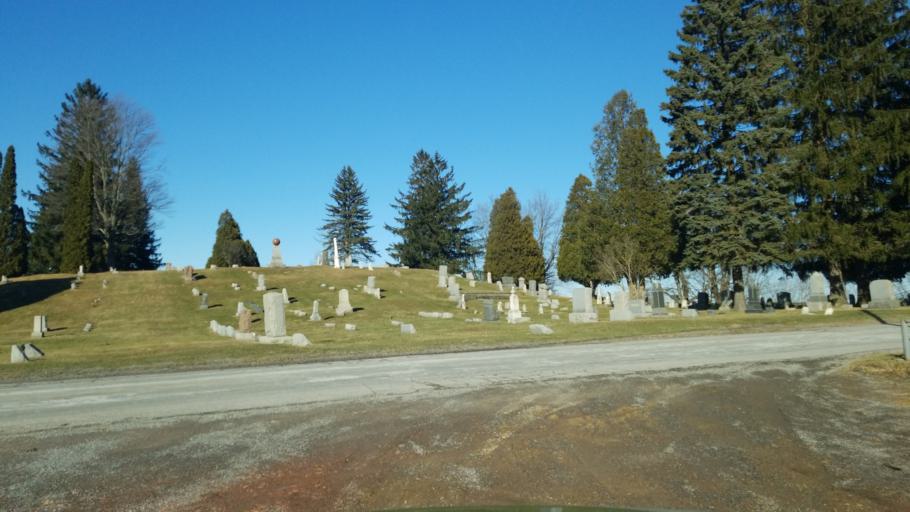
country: US
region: Pennsylvania
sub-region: Clearfield County
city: Sandy
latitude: 41.0539
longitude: -78.7238
